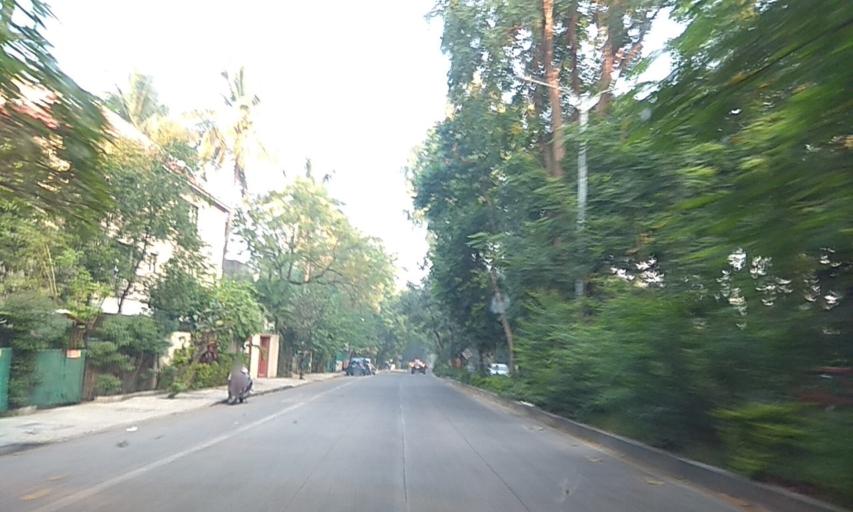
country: IN
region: Maharashtra
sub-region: Pune Division
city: Shivaji Nagar
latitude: 18.5414
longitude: 73.8175
